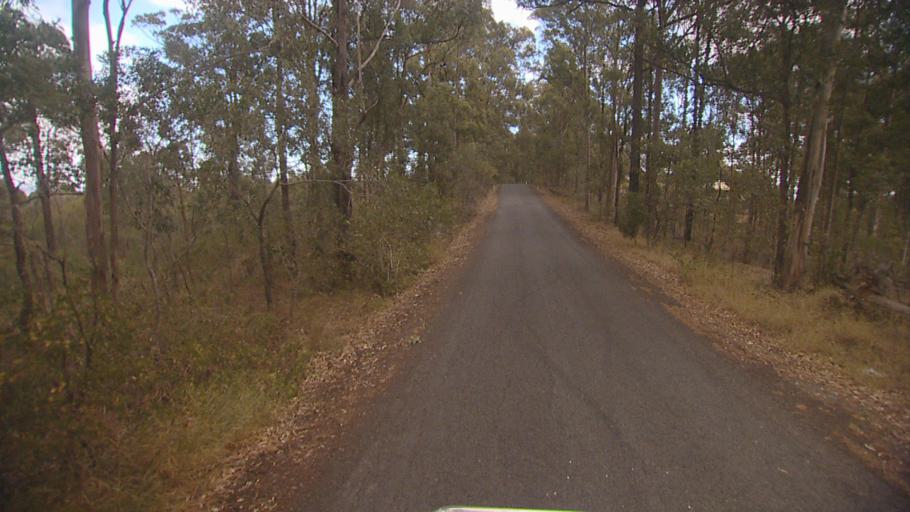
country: AU
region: Queensland
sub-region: Logan
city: Cedar Vale
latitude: -27.9000
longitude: 153.0367
